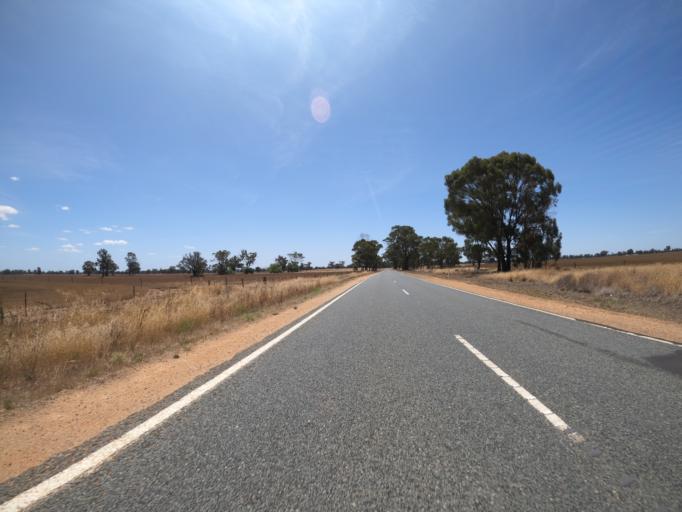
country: AU
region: Victoria
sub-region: Moira
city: Yarrawonga
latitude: -36.1963
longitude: 145.9670
